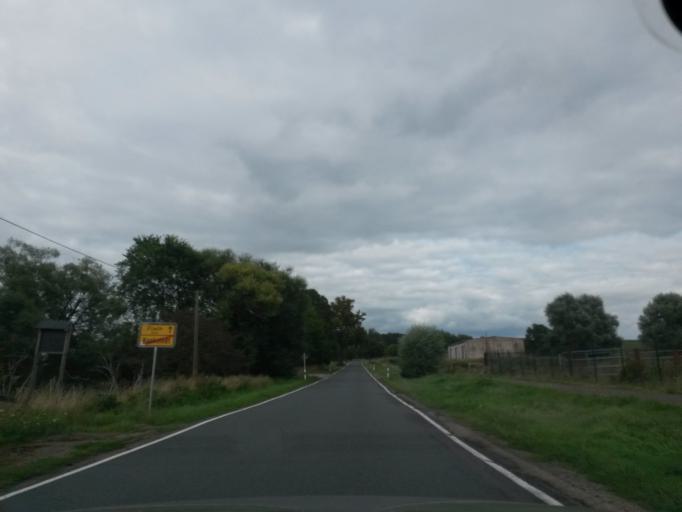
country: DE
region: Brandenburg
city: Gerswalde
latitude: 53.1740
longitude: 13.7776
